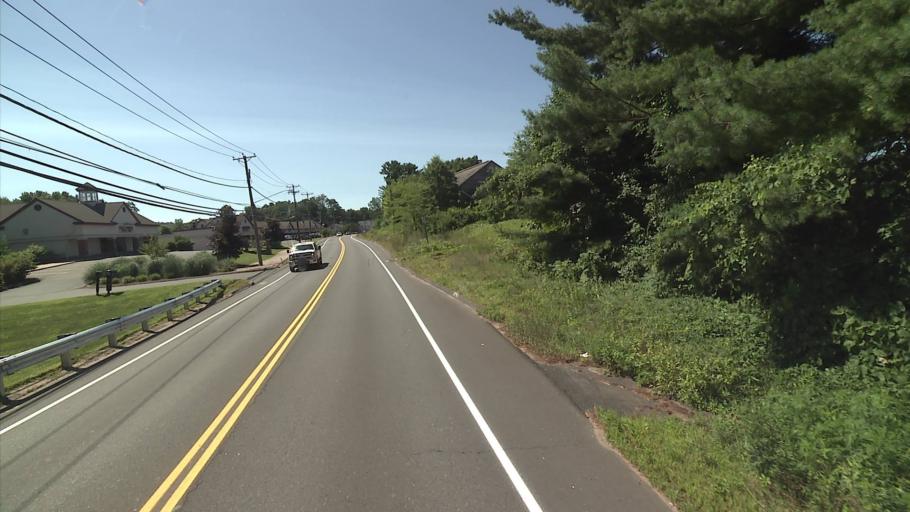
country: US
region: Connecticut
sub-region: Hartford County
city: Tariffville
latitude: 41.9054
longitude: -72.7870
